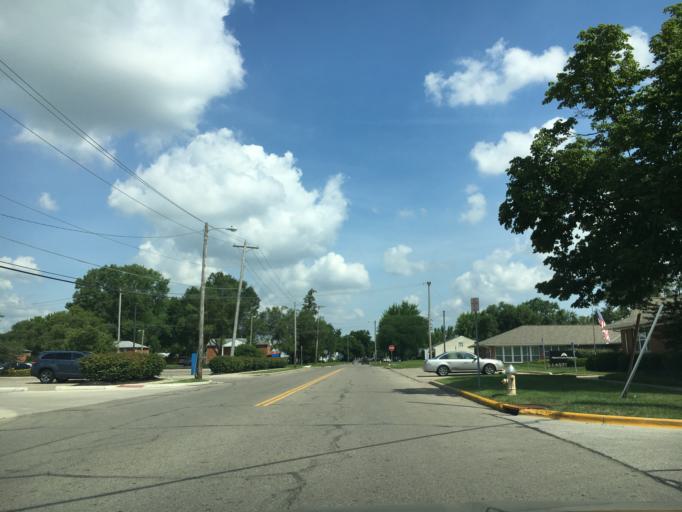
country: US
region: Ohio
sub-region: Franklin County
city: Lincoln Village
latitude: 39.9535
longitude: -83.1359
